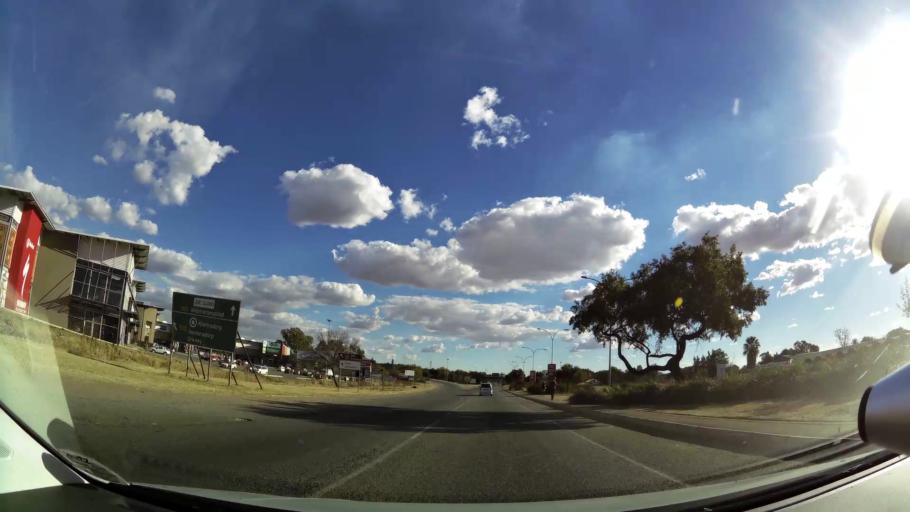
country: ZA
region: North-West
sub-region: Dr Kenneth Kaunda District Municipality
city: Klerksdorp
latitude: -26.8596
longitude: 26.6687
